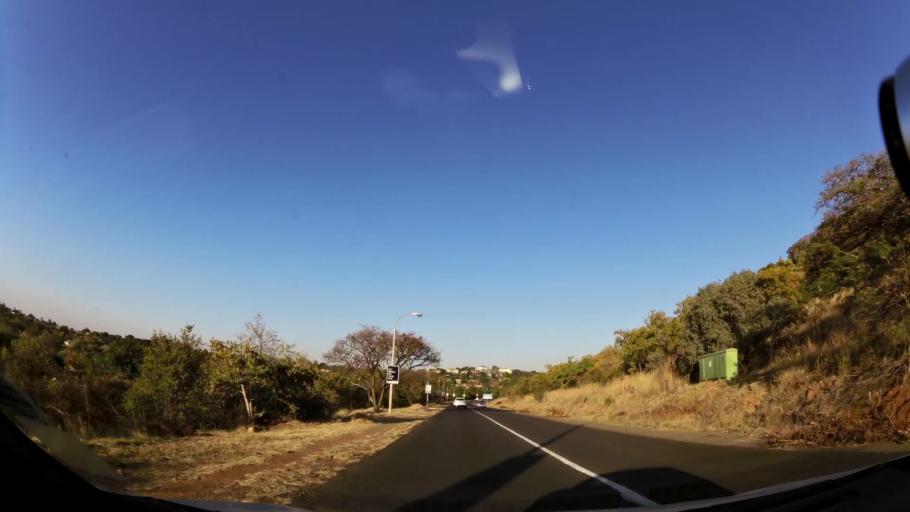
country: ZA
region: North-West
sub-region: Bojanala Platinum District Municipality
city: Rustenburg
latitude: -25.7039
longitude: 27.2345
